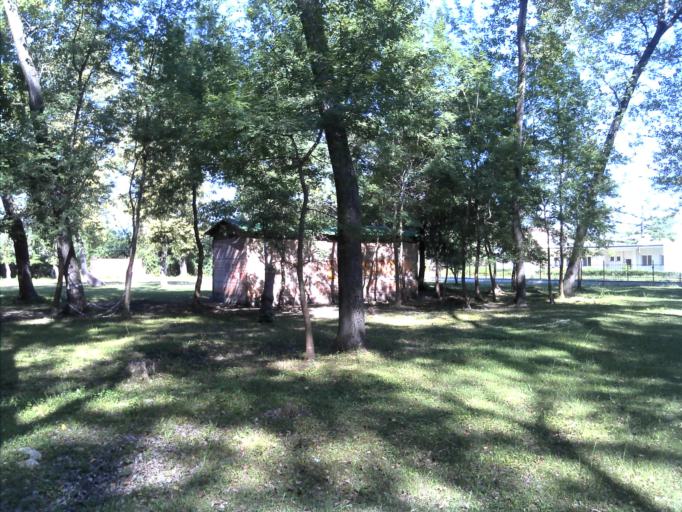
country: AL
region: Shkoder
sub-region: Rrethi i Shkodres
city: Velipoje
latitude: 41.8658
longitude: 19.4043
